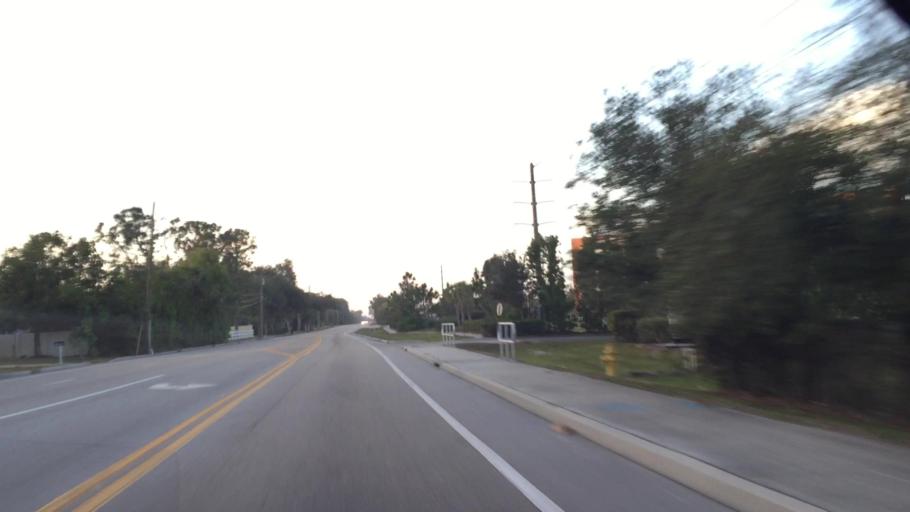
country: US
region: Florida
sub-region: Lee County
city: Pine Manor
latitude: 26.5824
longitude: -81.8473
